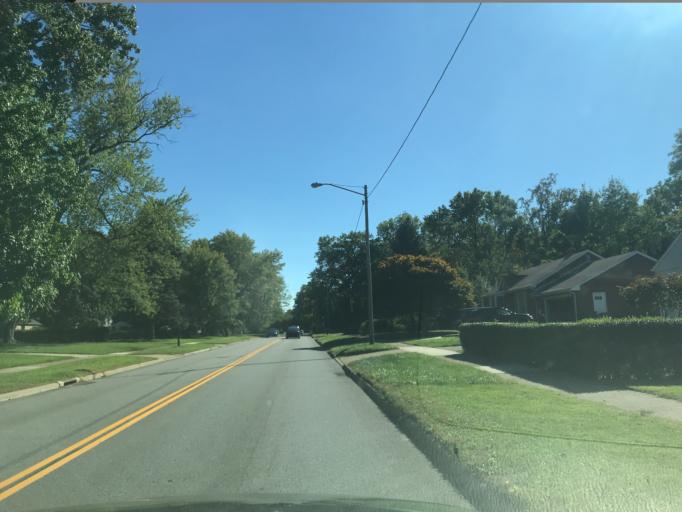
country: US
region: Ohio
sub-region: Lake County
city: Kirtland
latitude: 41.6492
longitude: -81.3755
